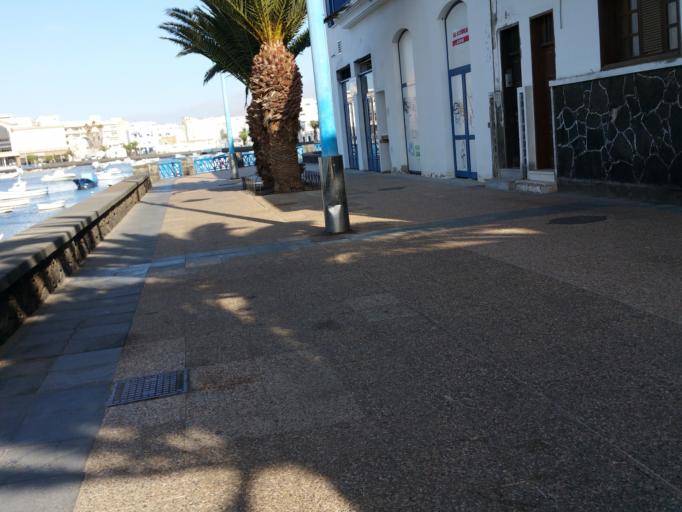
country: ES
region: Canary Islands
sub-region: Provincia de Las Palmas
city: Arrecife
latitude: 28.9615
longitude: -13.5453
